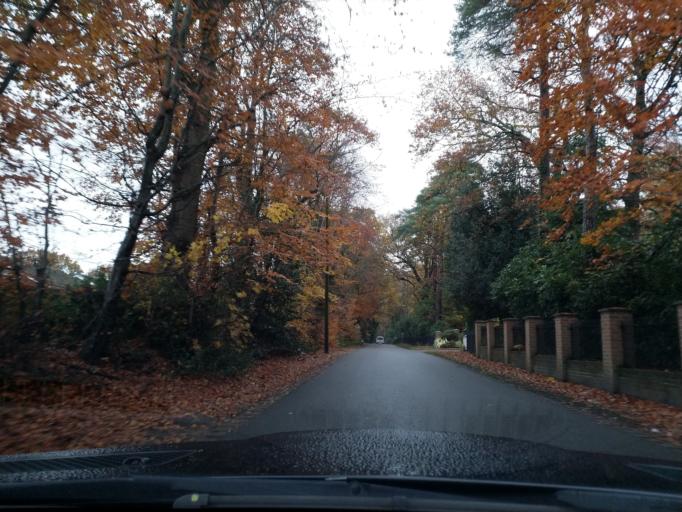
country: GB
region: England
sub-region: Surrey
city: Frimley
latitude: 51.3056
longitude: -0.7210
